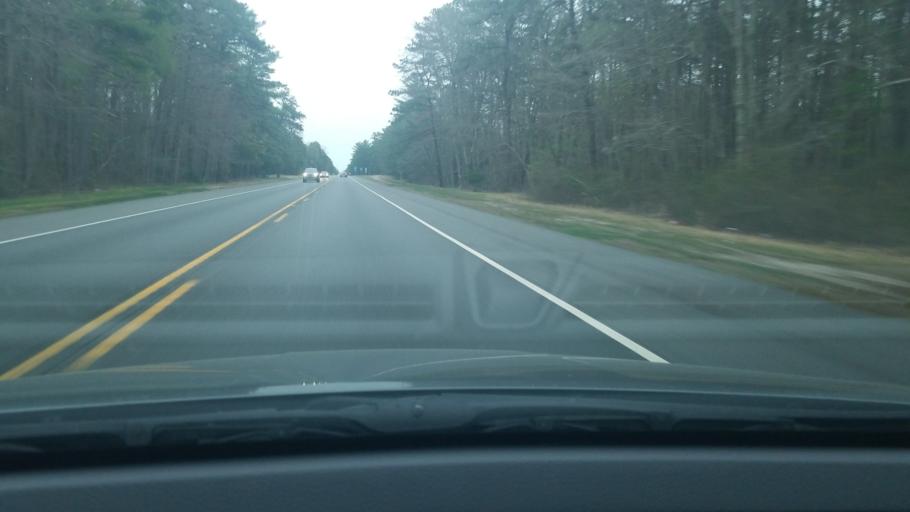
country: US
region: New Jersey
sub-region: Burlington County
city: Presidential Lakes Estates
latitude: 39.8934
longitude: -74.6149
